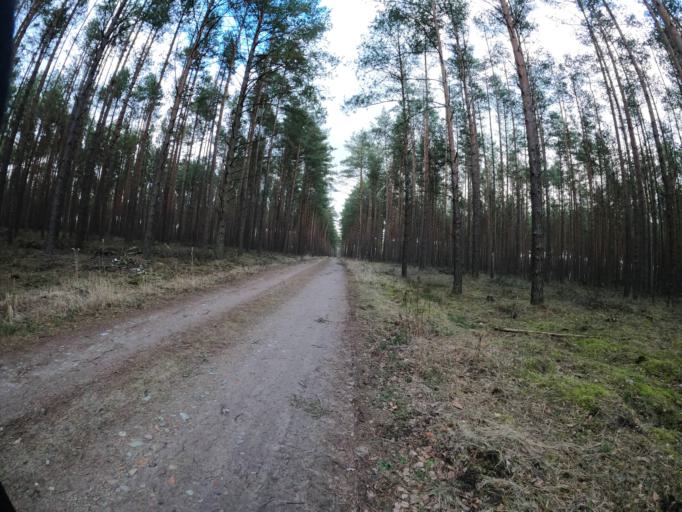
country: PL
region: Greater Poland Voivodeship
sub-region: Powiat zlotowski
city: Sypniewo
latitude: 53.4428
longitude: 16.5883
